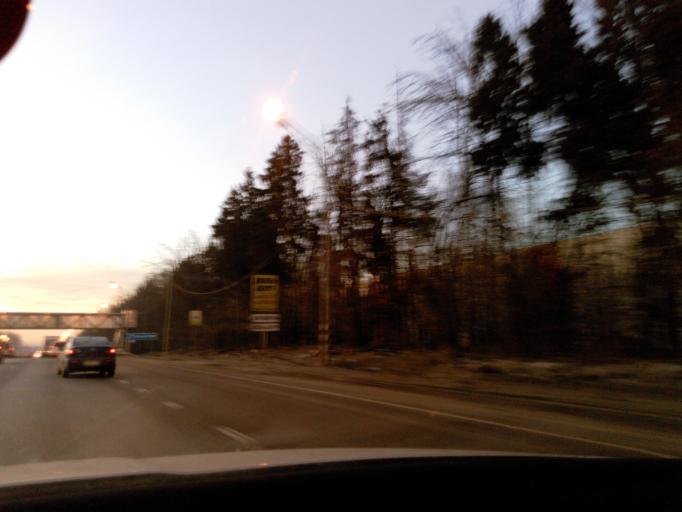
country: RU
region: Moskovskaya
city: Skhodnya
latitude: 55.9838
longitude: 37.2853
